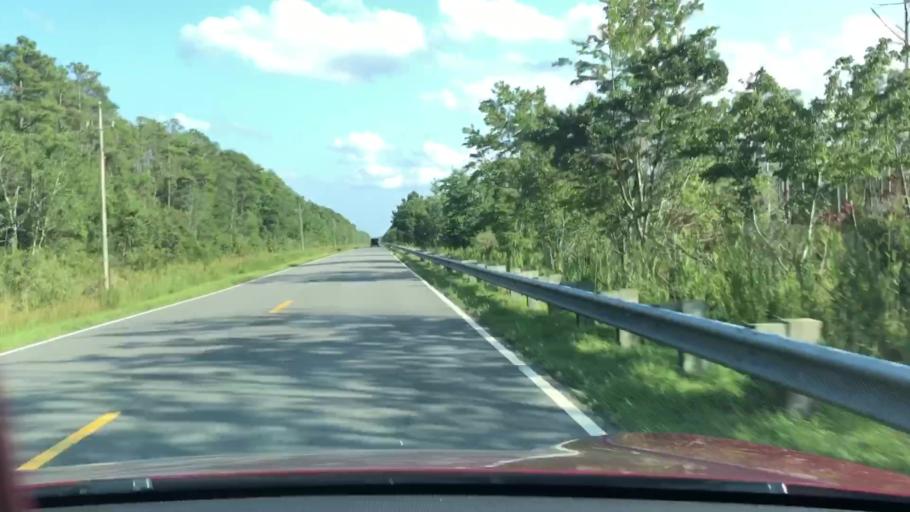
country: US
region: North Carolina
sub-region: Dare County
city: Manteo
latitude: 35.8055
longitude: -75.7863
